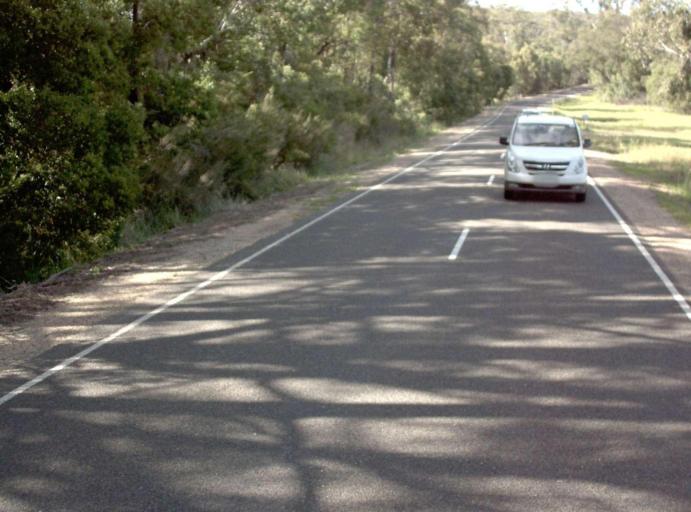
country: AU
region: Victoria
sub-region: East Gippsland
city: Lakes Entrance
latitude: -37.6065
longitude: 148.1194
